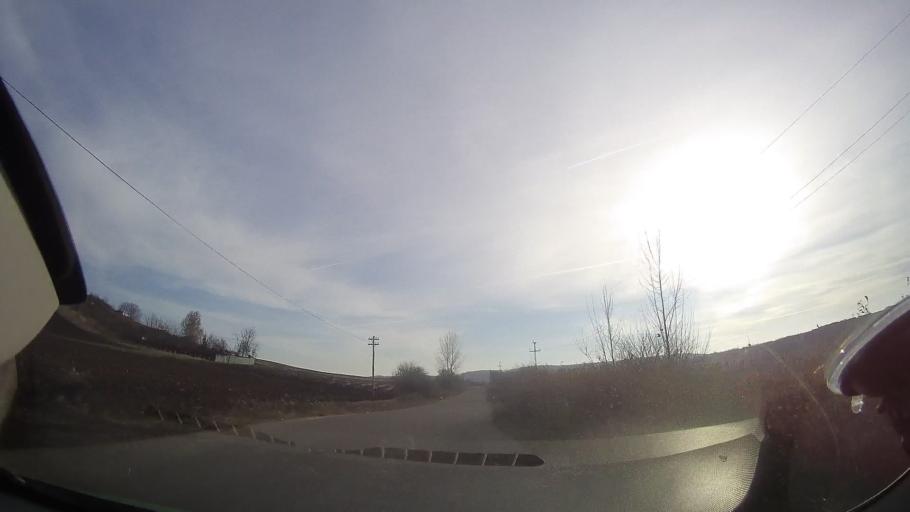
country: RO
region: Bihor
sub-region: Comuna Sarbi
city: Burzuc
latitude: 47.1630
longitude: 22.1629
